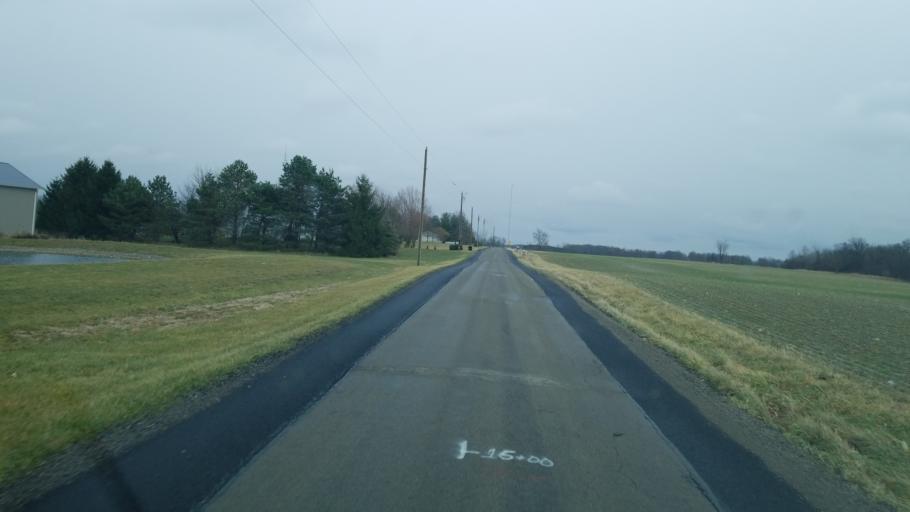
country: US
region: Ohio
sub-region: Union County
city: Marysville
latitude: 40.3054
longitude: -83.3474
